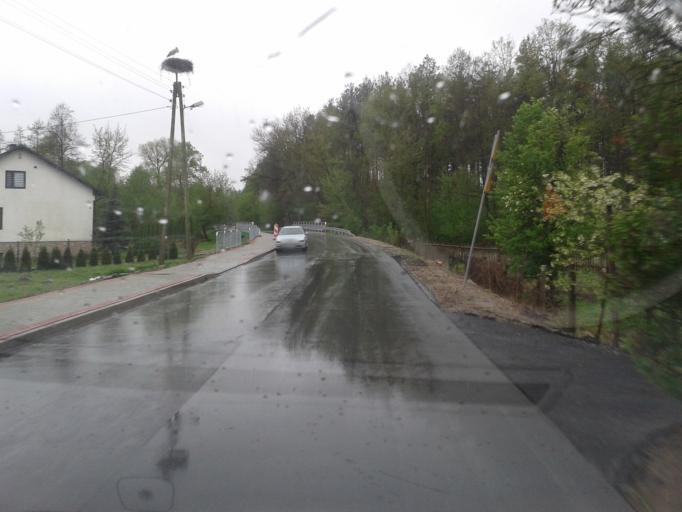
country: PL
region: Lublin Voivodeship
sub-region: Powiat tomaszowski
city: Lubycza Krolewska
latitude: 50.3619
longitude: 23.5413
